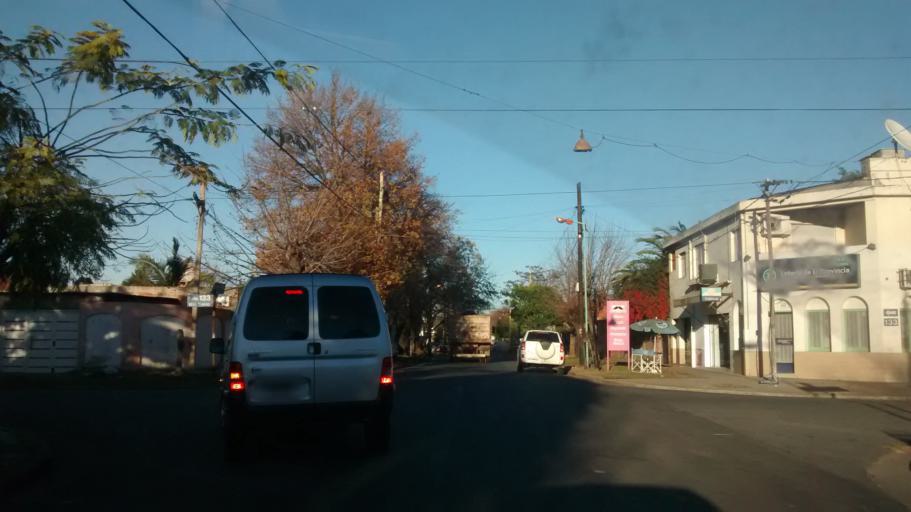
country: AR
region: Buenos Aires
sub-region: Partido de La Plata
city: La Plata
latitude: -34.9497
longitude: -57.9629
